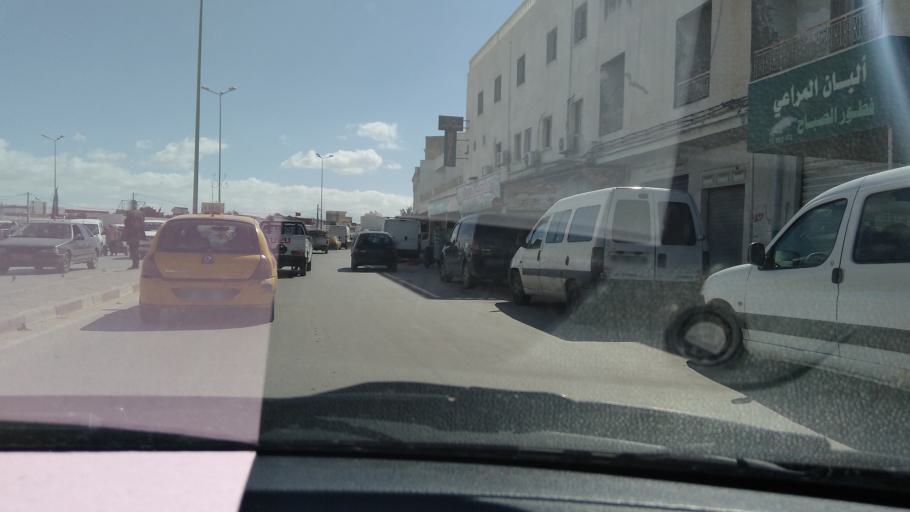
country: TN
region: Al Qayrawan
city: Kairouan
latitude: 35.6800
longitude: 10.0866
